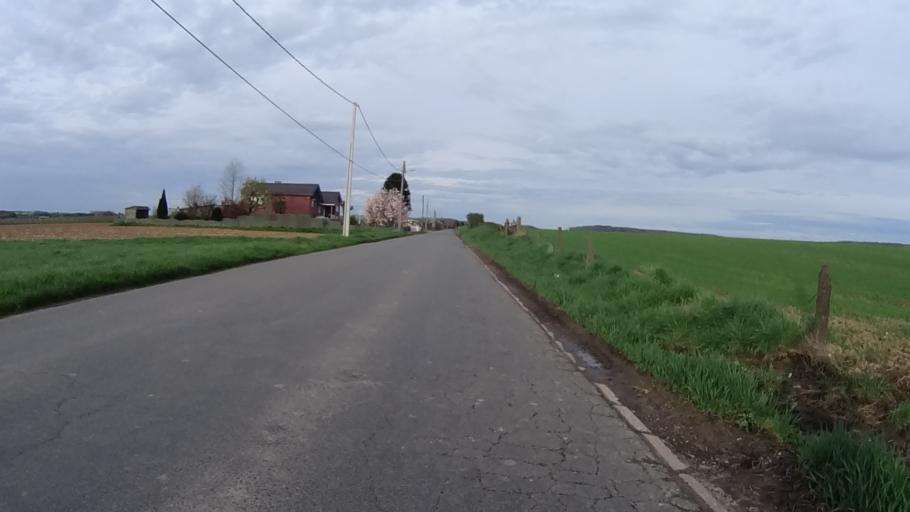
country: BE
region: Wallonia
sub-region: Province de Liege
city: Dalhem
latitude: 50.7454
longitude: 5.7398
